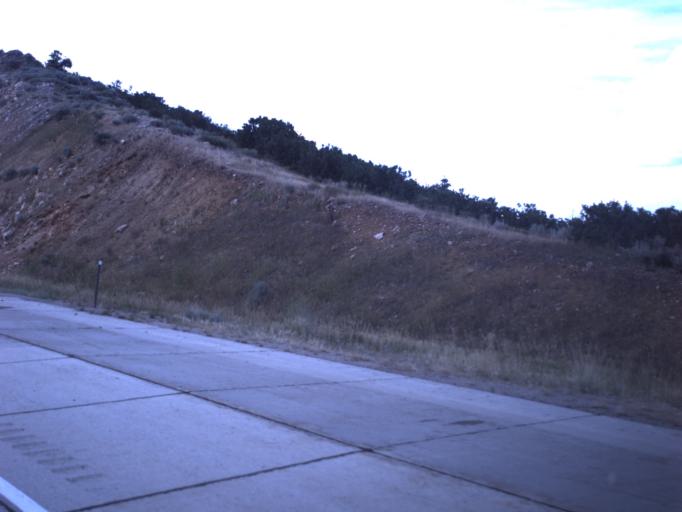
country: US
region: Utah
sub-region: Summit County
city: Park City
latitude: 40.6125
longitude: -111.4311
